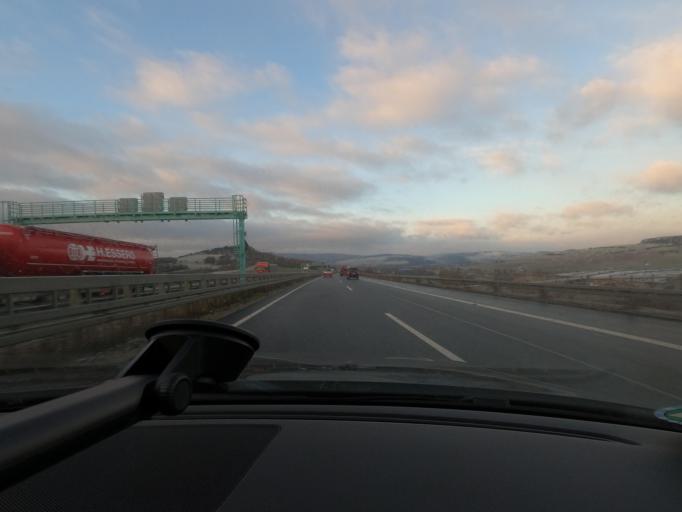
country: DE
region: Thuringia
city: Arenshausen
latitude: 51.3987
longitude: 9.9760
